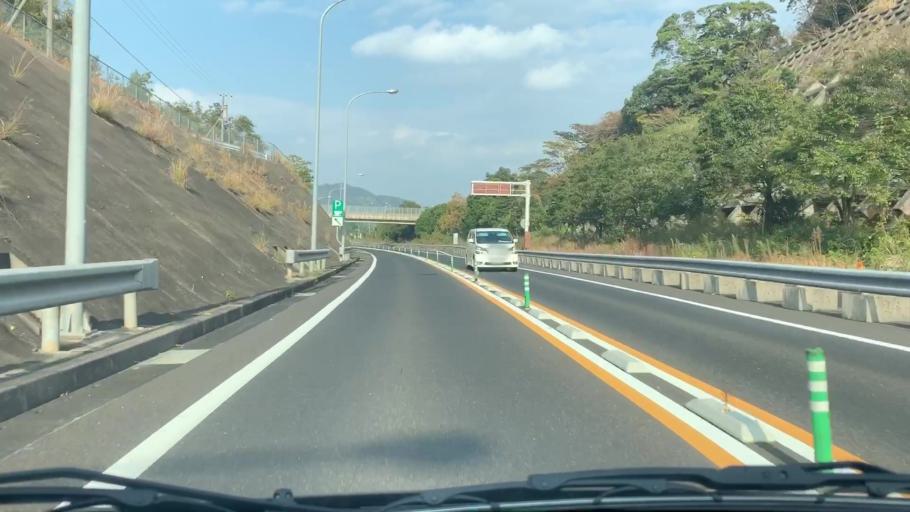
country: JP
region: Nagasaki
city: Sasebo
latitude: 33.0687
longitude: 129.7647
